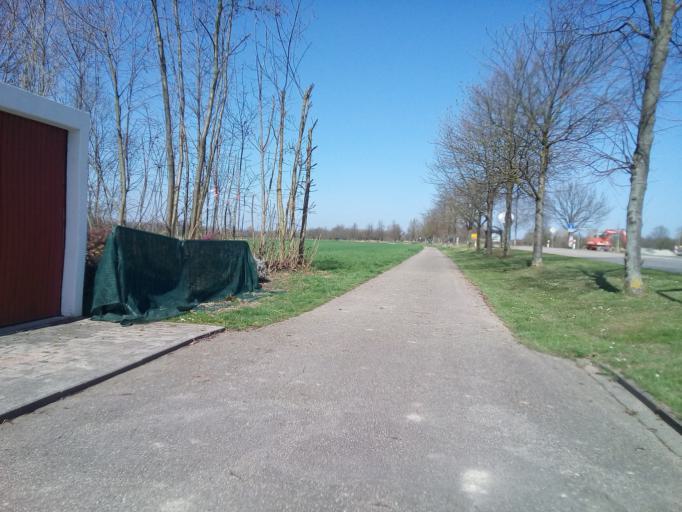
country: FR
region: Alsace
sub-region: Departement du Bas-Rhin
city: La Wantzenau
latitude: 48.6272
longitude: 7.8599
